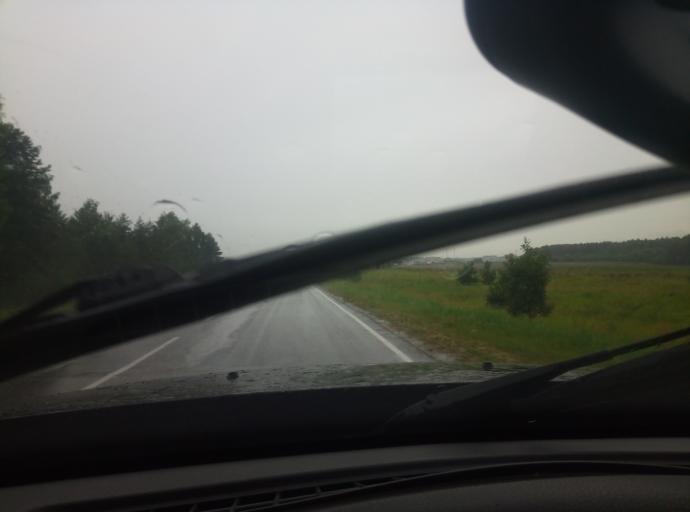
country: RU
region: Kaluga
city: Kremenki
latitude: 54.8773
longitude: 37.1442
